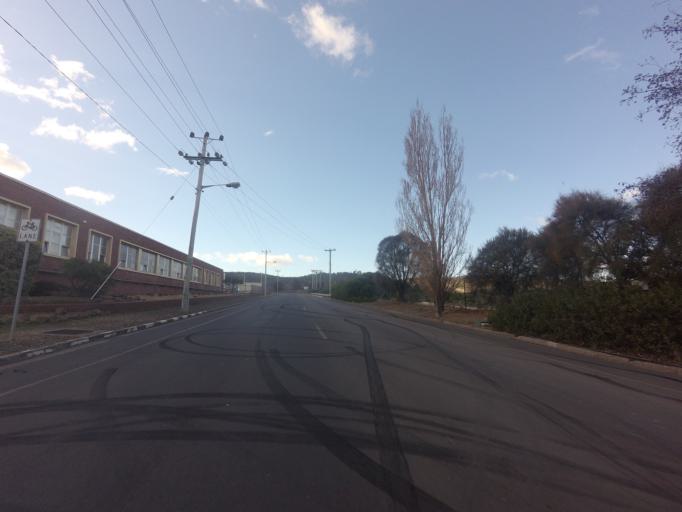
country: AU
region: Tasmania
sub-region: Glenorchy
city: Lutana
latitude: -42.8372
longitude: 147.3205
